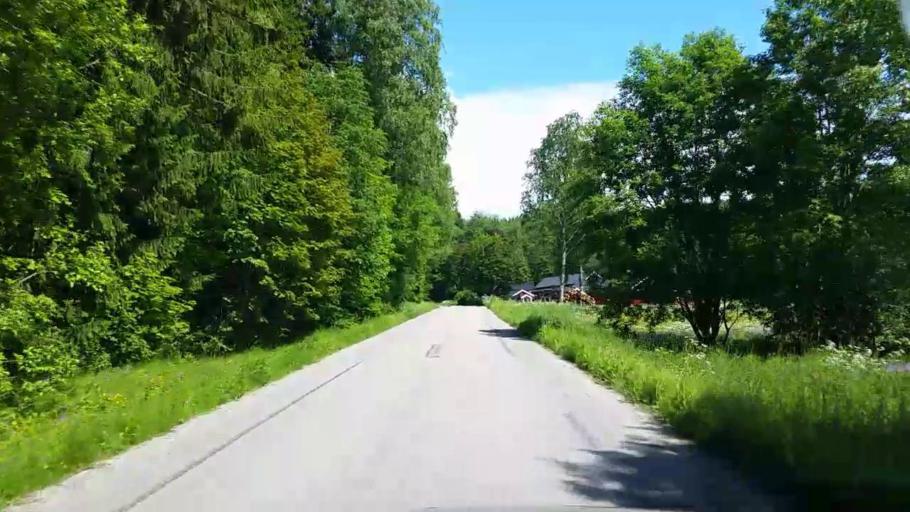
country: SE
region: Vaestmanland
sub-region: Fagersta Kommun
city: Fagersta
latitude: 59.9781
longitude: 15.7441
